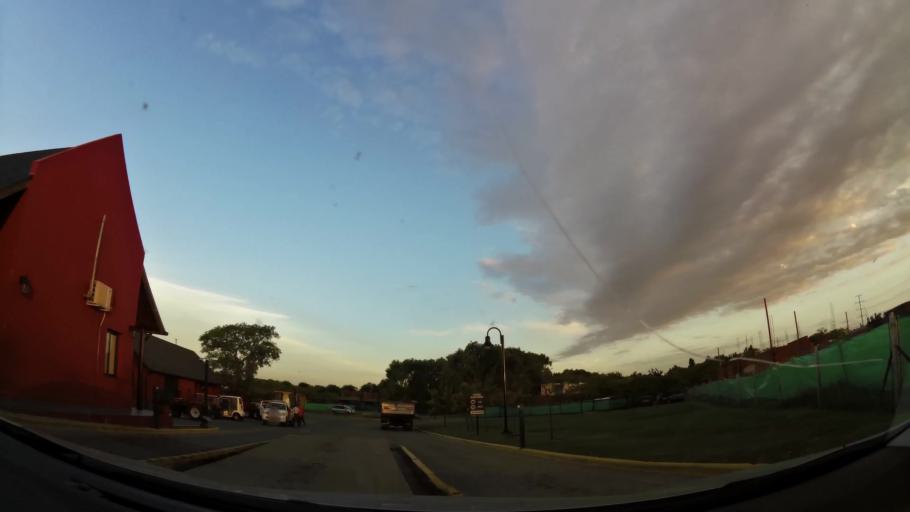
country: AR
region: Buenos Aires
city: Santa Catalina - Dique Lujan
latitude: -34.4392
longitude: -58.6583
